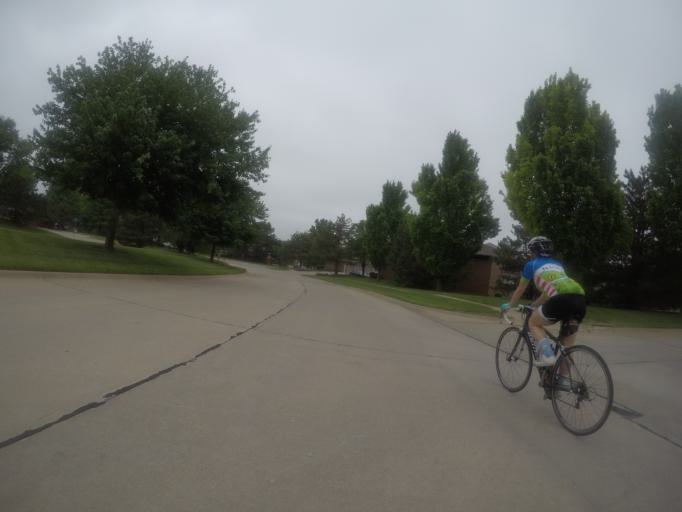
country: US
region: Kansas
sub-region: Riley County
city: Manhattan
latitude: 39.1945
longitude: -96.6036
